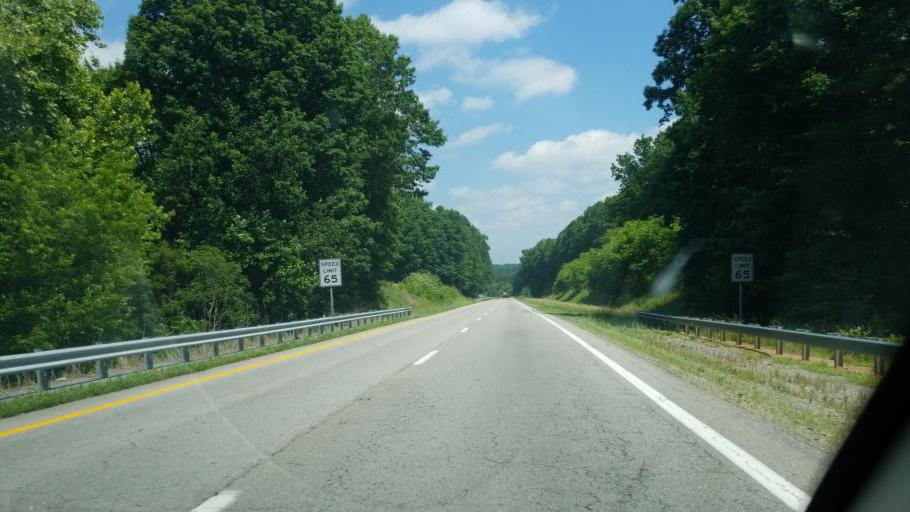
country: US
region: Virginia
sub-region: Pittsylvania County
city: Motley
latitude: 37.0868
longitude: -79.3320
